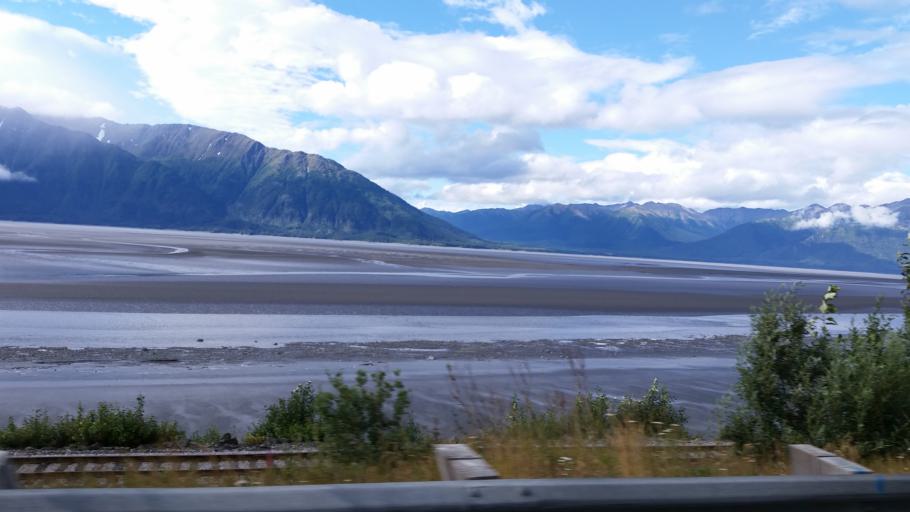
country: US
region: Alaska
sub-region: Anchorage Municipality
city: Elmendorf Air Force Base
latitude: 60.9869
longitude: -149.5156
